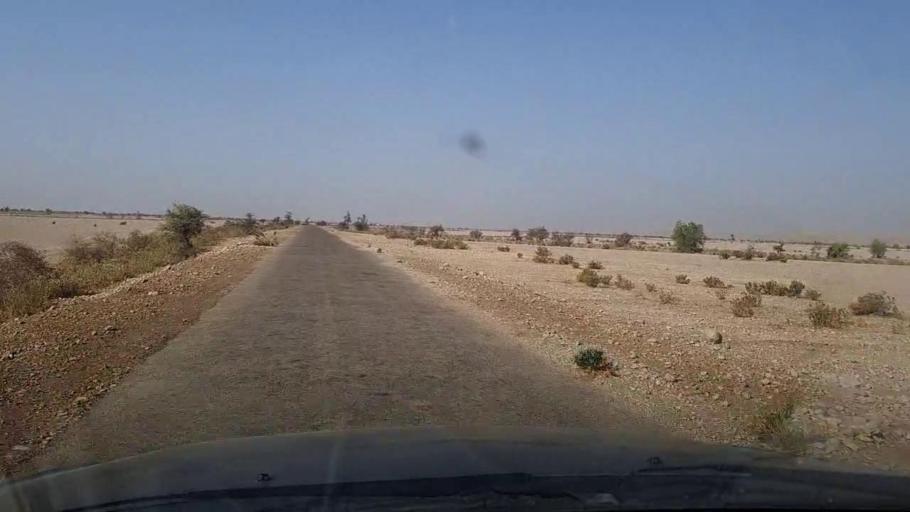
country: PK
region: Sindh
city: Sann
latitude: 25.9091
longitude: 68.0067
